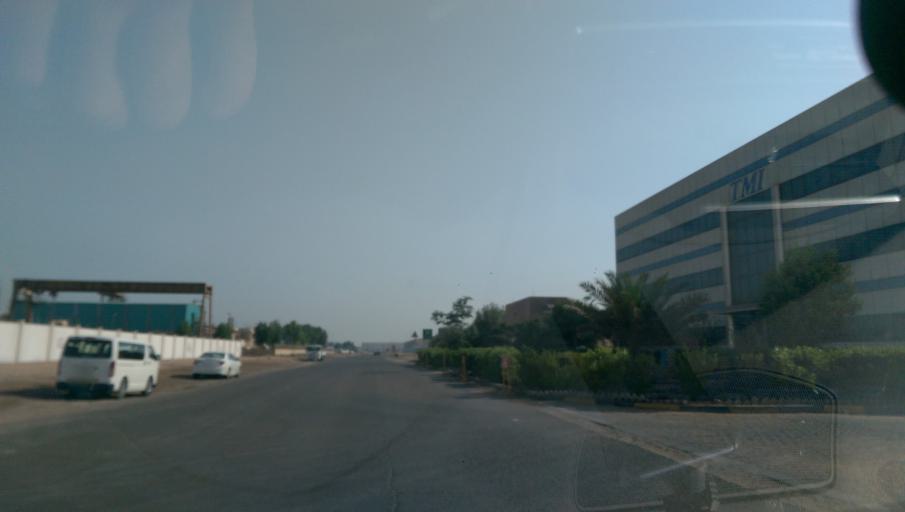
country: AE
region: Abu Dhabi
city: Abu Dhabi
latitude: 24.3241
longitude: 54.4773
